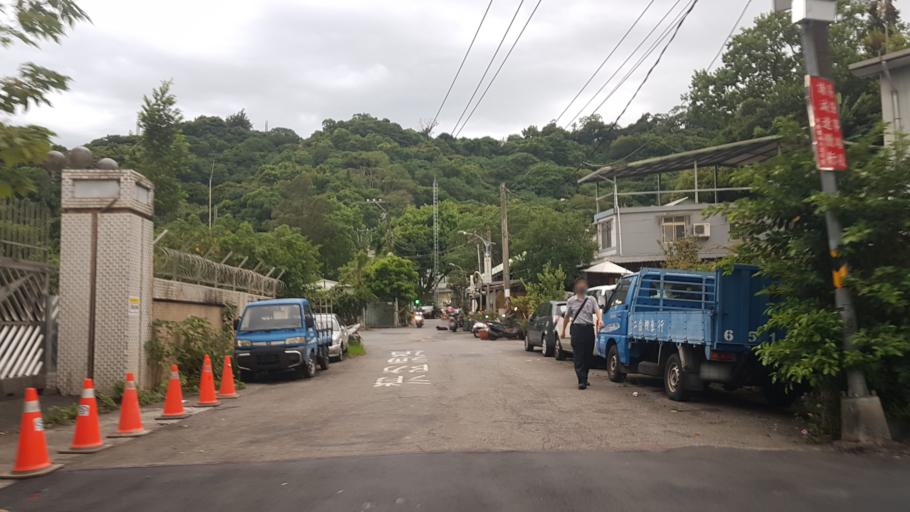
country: TW
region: Taipei
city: Taipei
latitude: 25.0116
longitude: 121.5458
